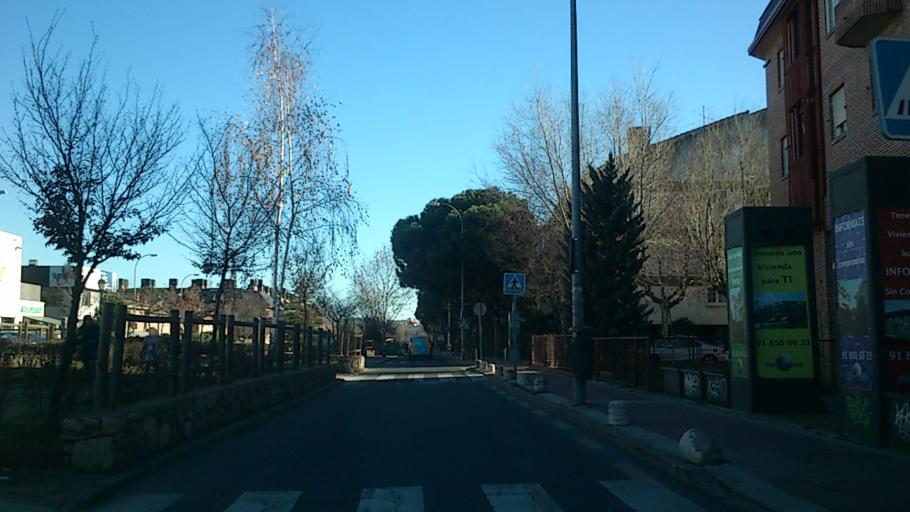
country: ES
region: Madrid
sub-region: Provincia de Madrid
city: Collado-Villalba
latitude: 40.6360
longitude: -4.0173
